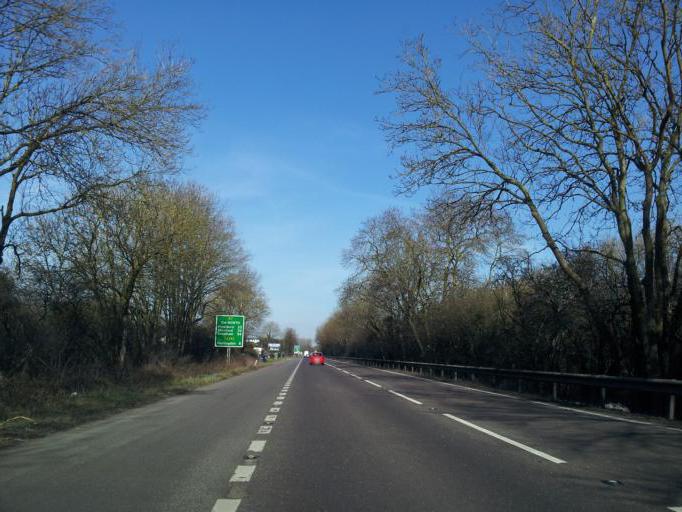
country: GB
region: England
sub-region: Cambridgeshire
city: Little Paxton
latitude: 52.2575
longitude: -0.2639
